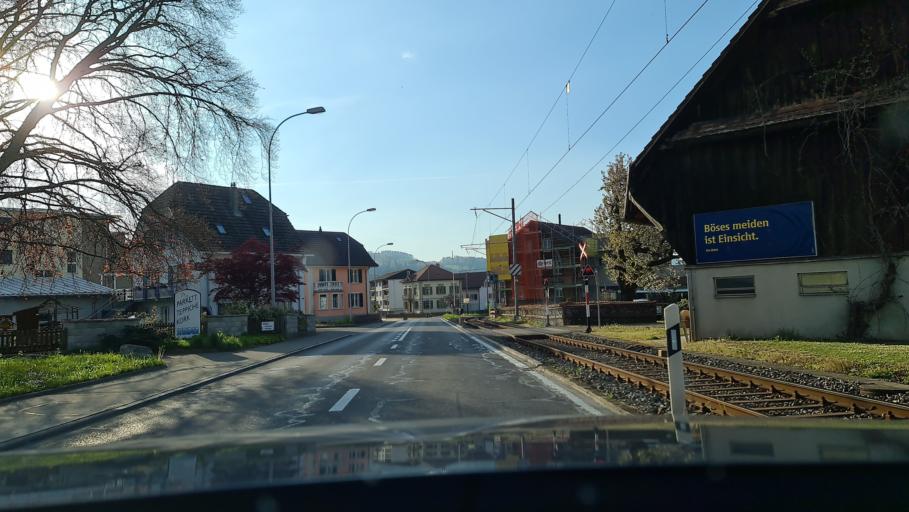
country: CH
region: Lucerne
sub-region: Hochdorf District
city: Hitzkirch
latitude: 47.2269
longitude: 8.2457
